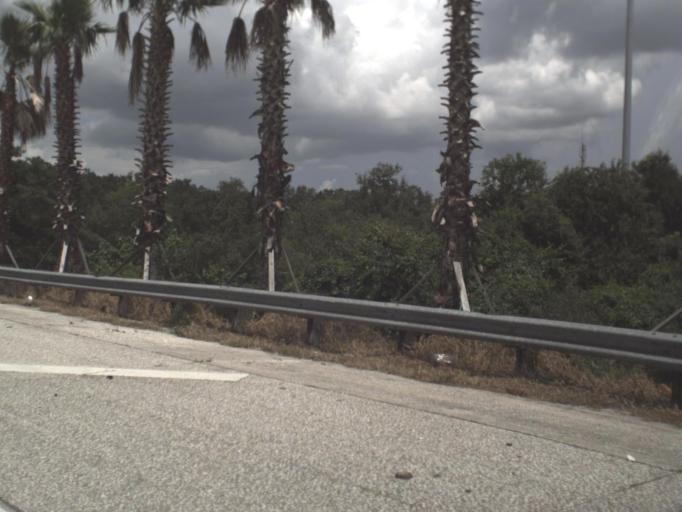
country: US
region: Florida
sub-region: Hillsborough County
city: Mango
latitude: 27.9979
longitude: -82.3264
